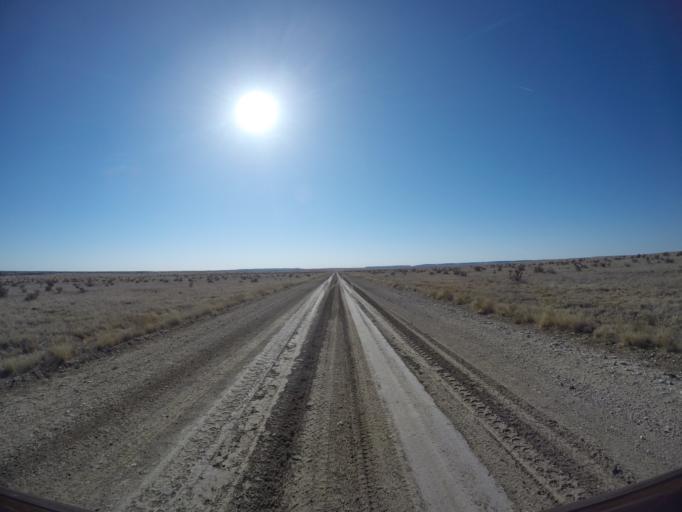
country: US
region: Colorado
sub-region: Otero County
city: La Junta
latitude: 37.7261
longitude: -103.6205
